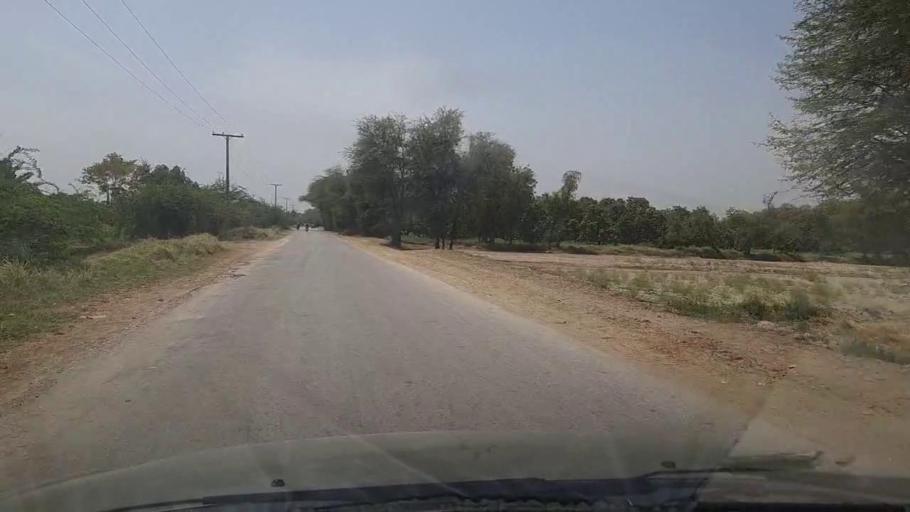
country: PK
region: Sindh
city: Bhiria
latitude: 26.8984
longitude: 68.2223
